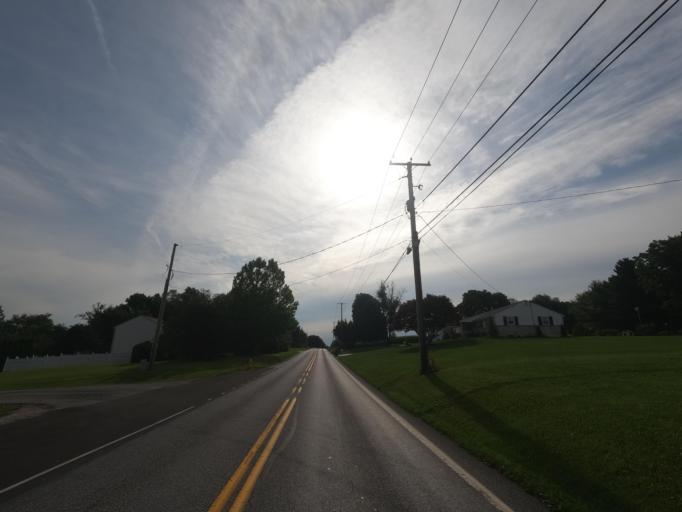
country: US
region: Pennsylvania
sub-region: York County
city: Shrewsbury
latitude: 39.7854
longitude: -76.6594
